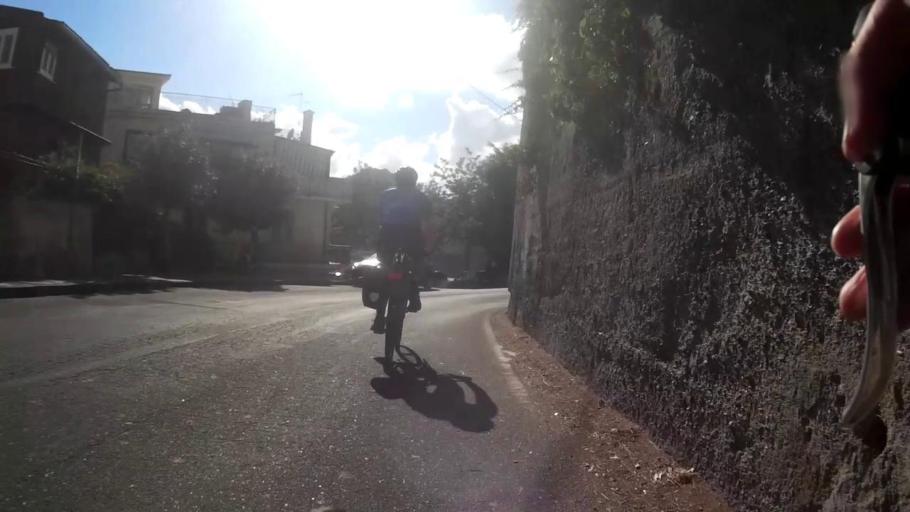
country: IT
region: Sicily
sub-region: Messina
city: Castelmola
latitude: 37.8537
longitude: 15.2800
